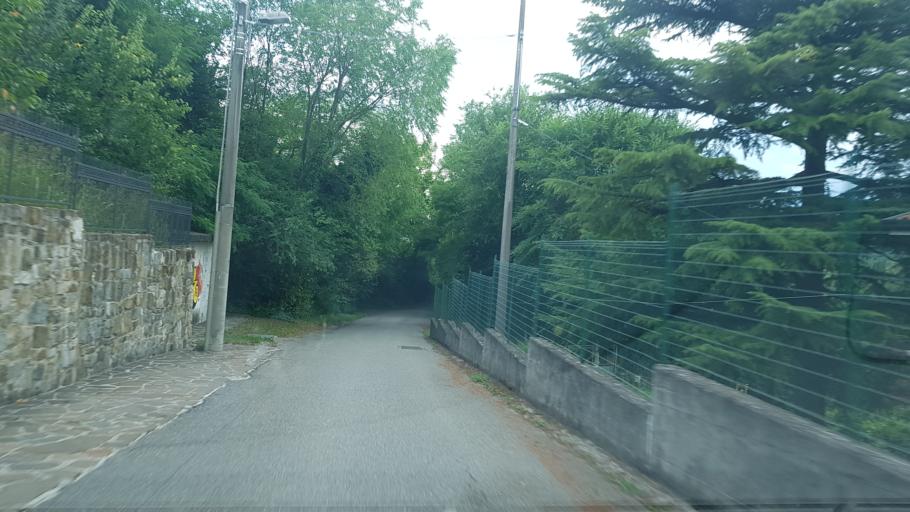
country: IT
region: Friuli Venezia Giulia
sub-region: Provincia di Gorizia
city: Gorizia
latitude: 45.9580
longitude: 13.6186
